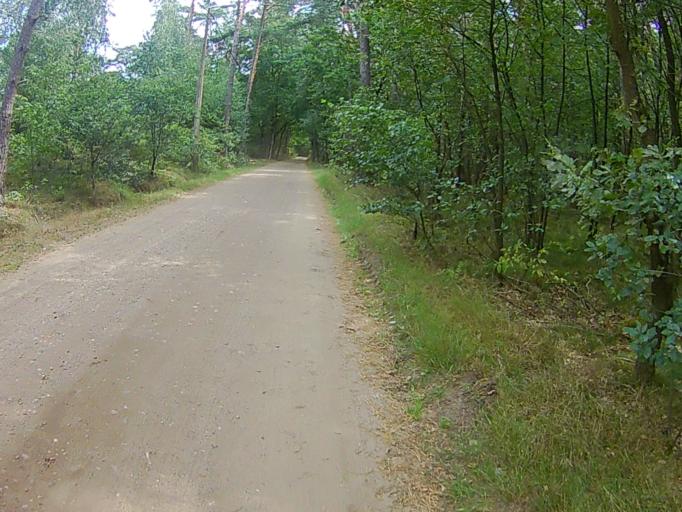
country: BE
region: Flanders
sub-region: Provincie Antwerpen
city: Herentals
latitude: 51.2150
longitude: 4.8769
